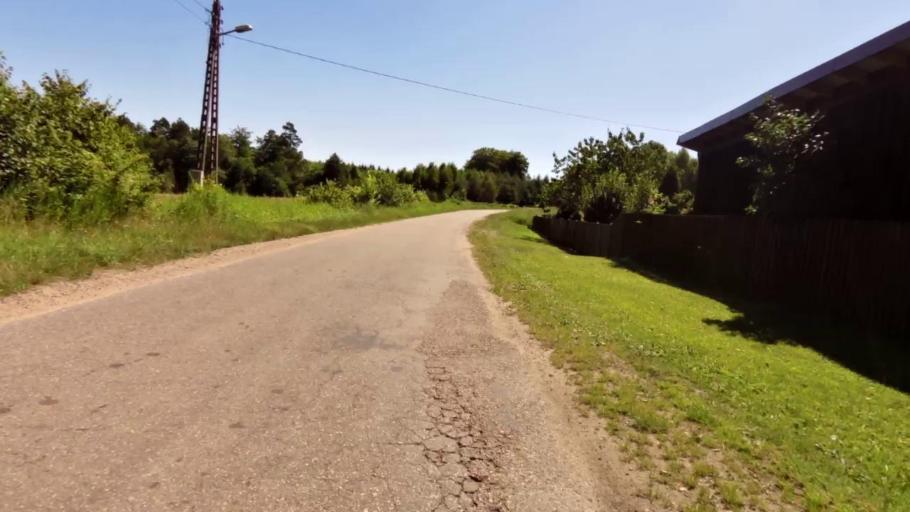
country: PL
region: West Pomeranian Voivodeship
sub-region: Powiat szczecinecki
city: Bialy Bor
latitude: 53.9461
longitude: 16.8538
